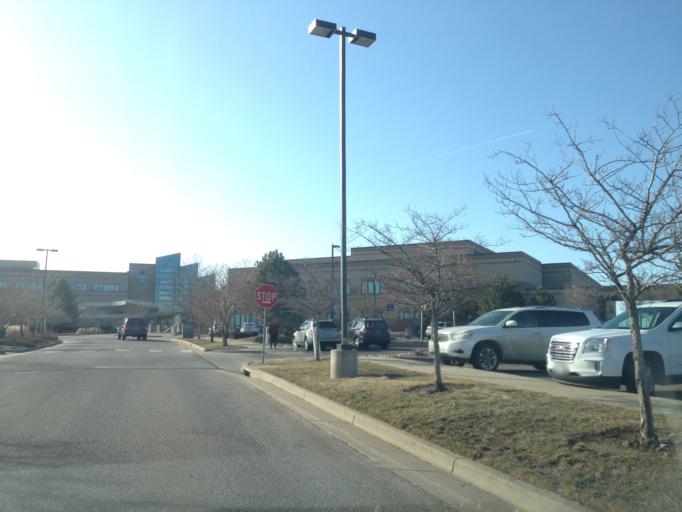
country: US
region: Colorado
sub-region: Boulder County
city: Superior
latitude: 39.9512
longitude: -105.1507
